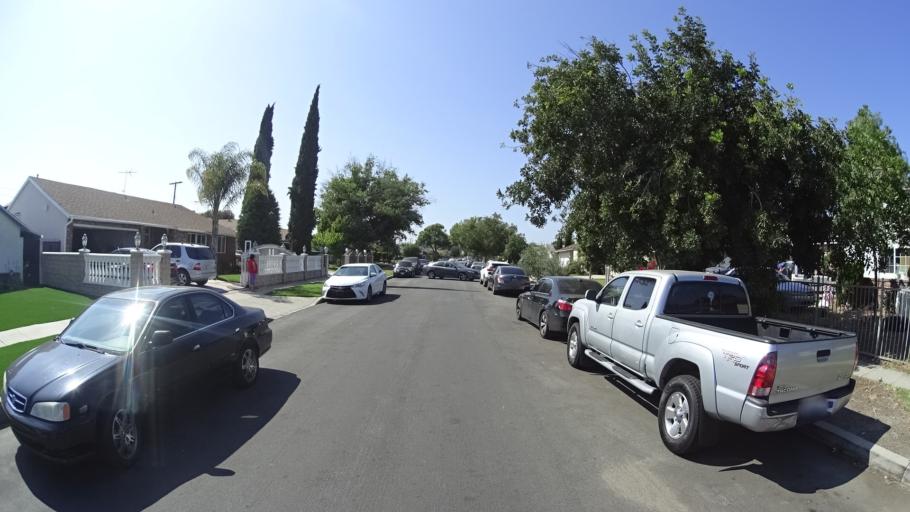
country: US
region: California
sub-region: Los Angeles County
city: Van Nuys
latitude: 34.1981
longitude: -118.4244
